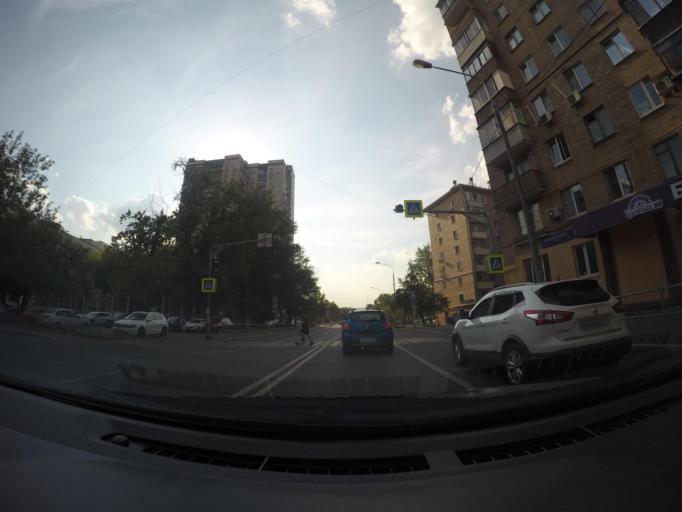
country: RU
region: Moscow
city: Lefortovo
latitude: 55.7793
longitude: 37.7239
